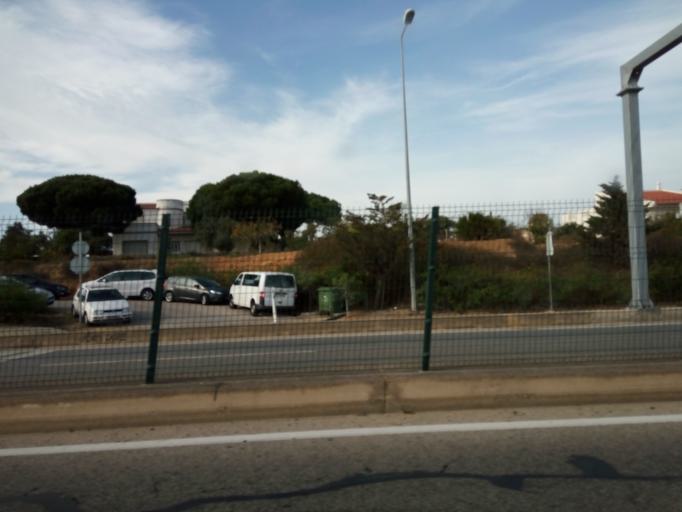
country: PT
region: Faro
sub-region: Faro
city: Faro
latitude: 37.0249
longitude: -7.9698
